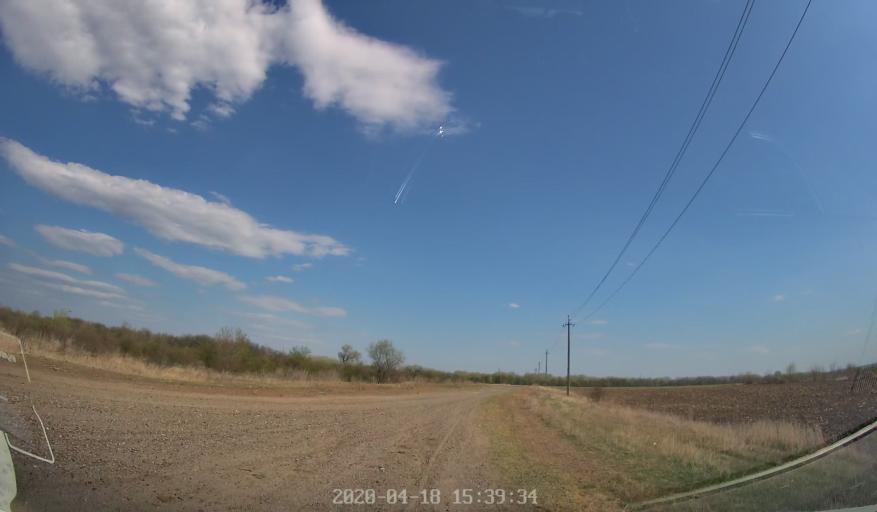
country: MD
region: Chisinau
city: Vadul lui Voda
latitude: 47.1463
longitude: 29.0891
